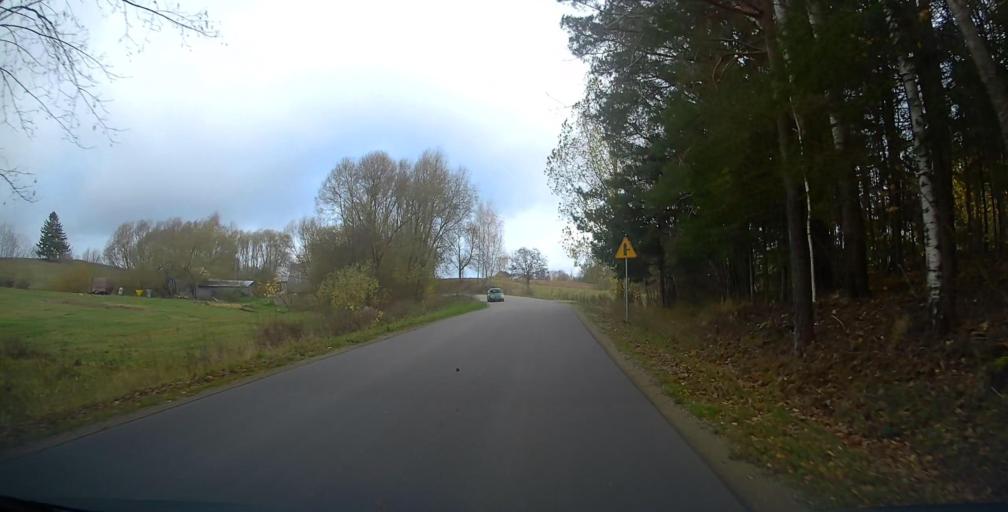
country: PL
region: Podlasie
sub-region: Suwalki
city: Suwalki
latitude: 54.3102
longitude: 22.8807
